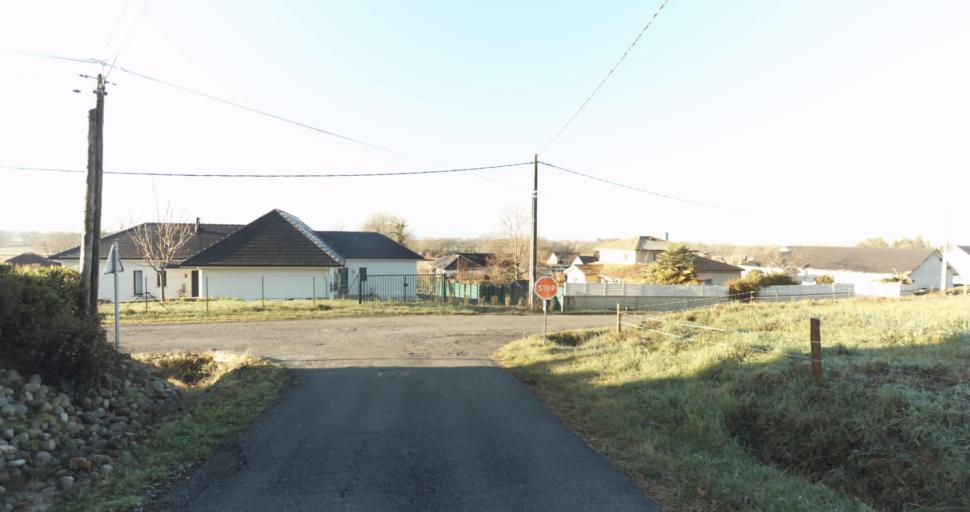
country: FR
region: Aquitaine
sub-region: Departement des Pyrenees-Atlantiques
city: Morlaas
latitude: 43.3287
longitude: -0.2778
